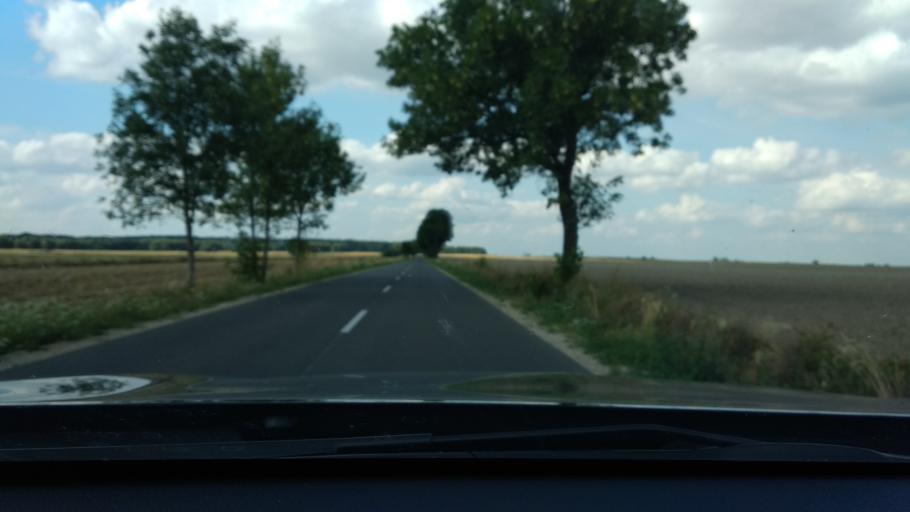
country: PL
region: Masovian Voivodeship
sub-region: Powiat pultuski
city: Zatory
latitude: 52.5631
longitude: 21.1869
